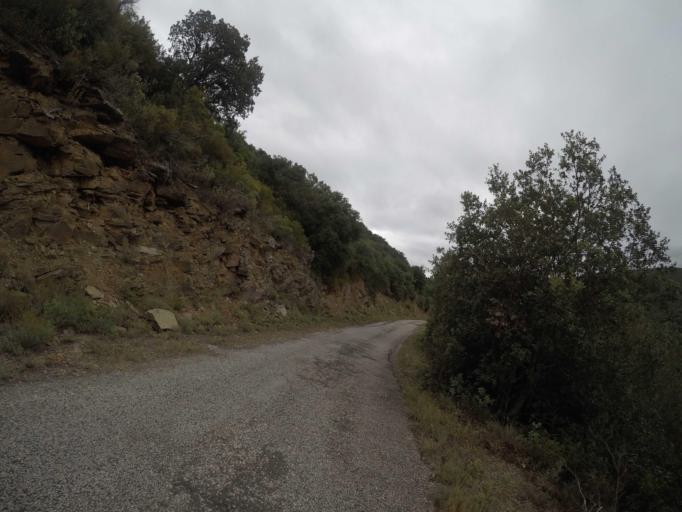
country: FR
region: Languedoc-Roussillon
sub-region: Departement des Pyrenees-Orientales
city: Ille-sur-Tet
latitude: 42.6135
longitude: 2.6055
